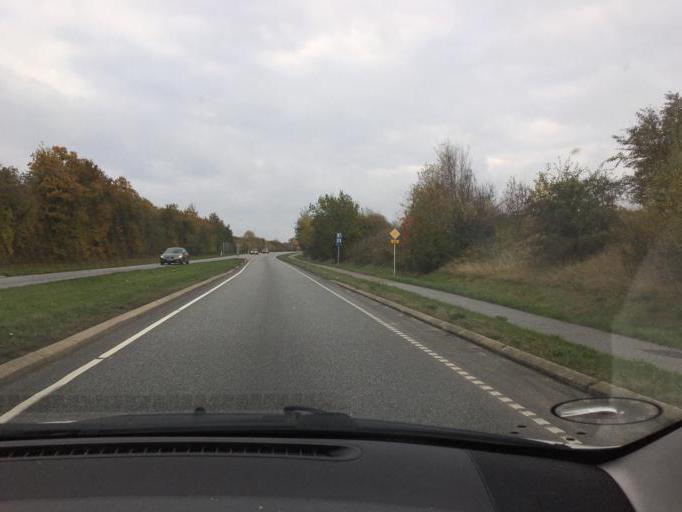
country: DK
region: South Denmark
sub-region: Fredericia Kommune
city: Fredericia
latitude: 55.6076
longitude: 9.7561
